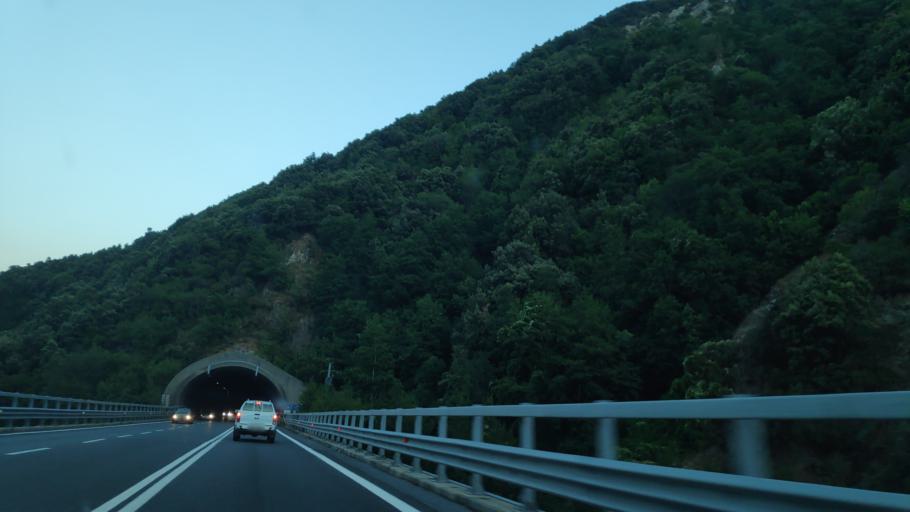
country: IT
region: Calabria
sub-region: Provincia di Reggio Calabria
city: Canolo
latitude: 38.3663
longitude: 16.1853
